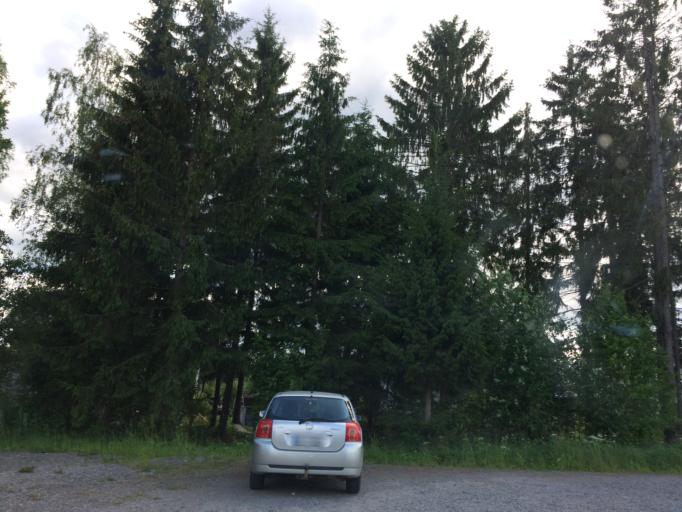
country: FI
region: Haeme
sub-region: Haemeenlinna
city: Parola
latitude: 60.9786
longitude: 24.3736
